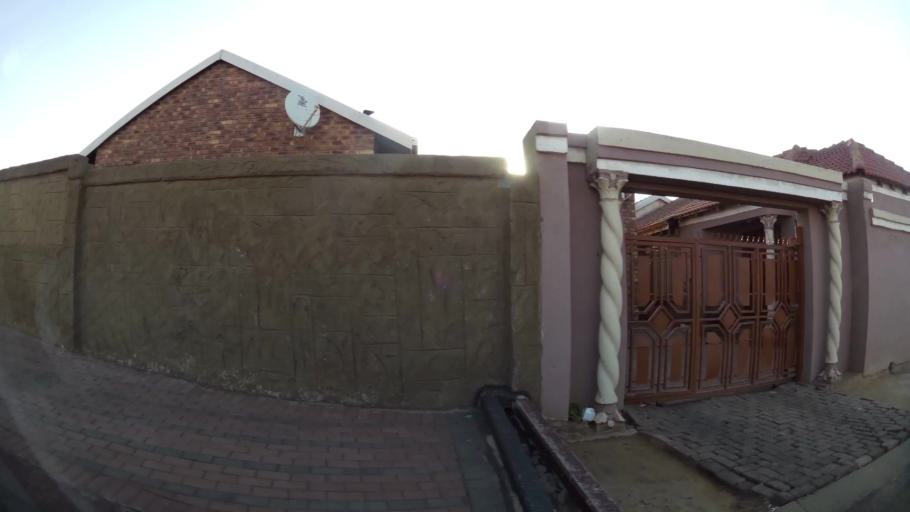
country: ZA
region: Gauteng
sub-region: Ekurhuleni Metropolitan Municipality
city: Tembisa
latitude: -26.0118
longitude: 28.2301
